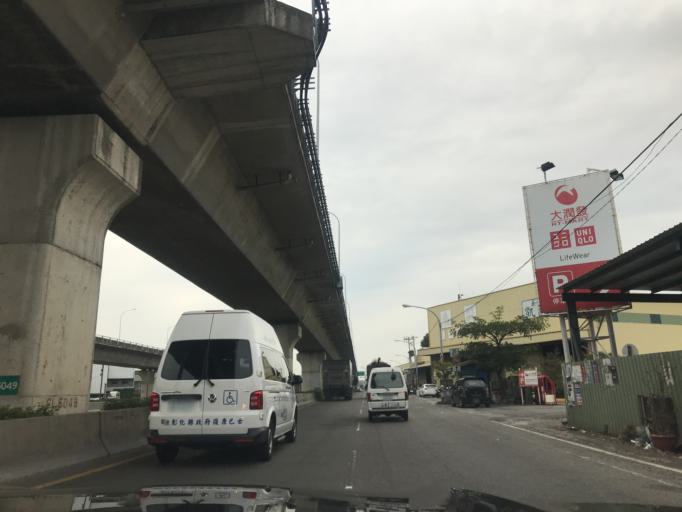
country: TW
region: Taiwan
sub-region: Nantou
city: Nantou
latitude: 23.9463
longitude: 120.5623
